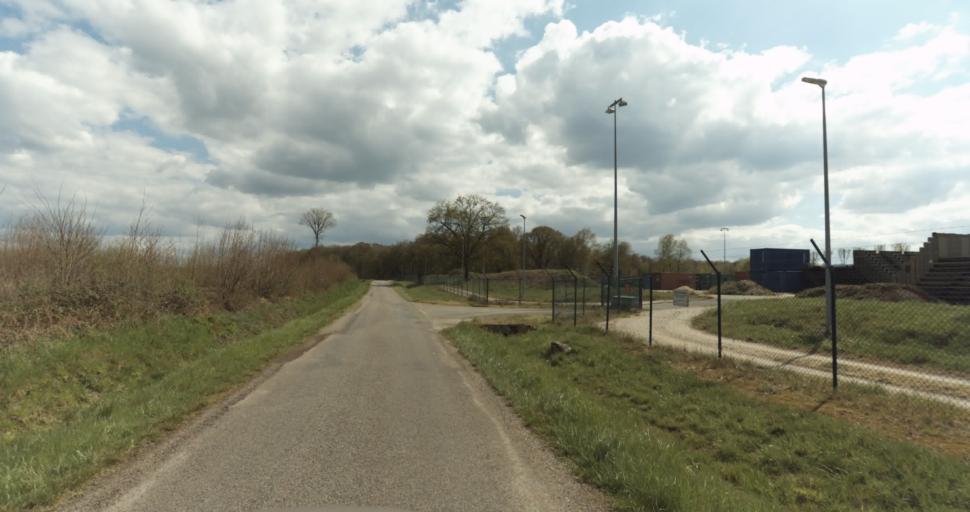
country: FR
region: Bourgogne
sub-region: Departement de la Cote-d'Or
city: Auxonne
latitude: 47.1773
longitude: 5.4093
